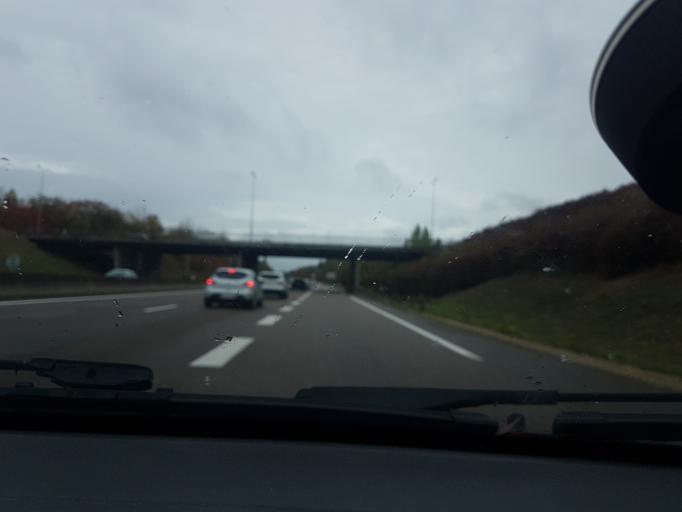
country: FR
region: Bourgogne
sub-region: Departement de la Cote-d'Or
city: Saint-Apollinaire
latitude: 47.3293
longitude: 5.0764
